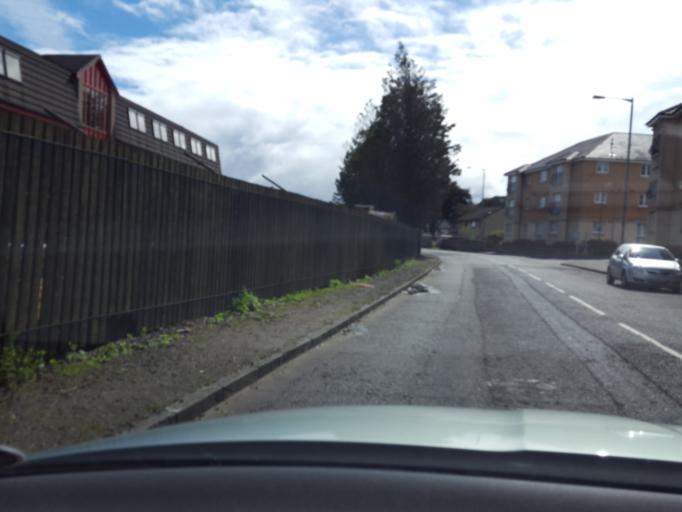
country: GB
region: Scotland
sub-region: Falkirk
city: Bo'ness
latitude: 56.0159
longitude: -3.5804
